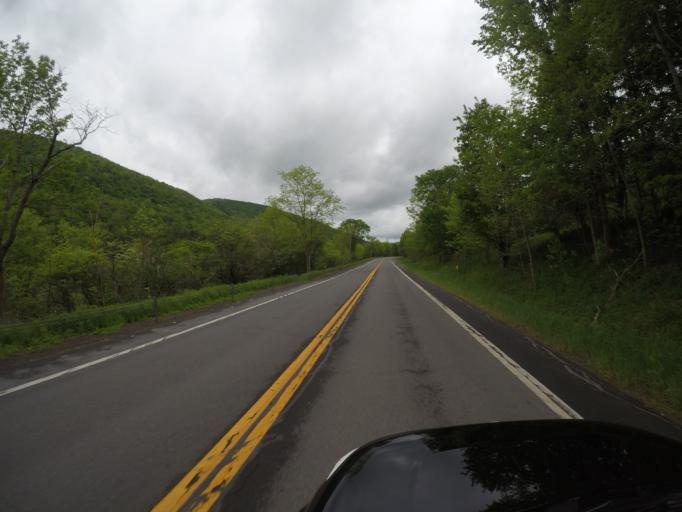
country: US
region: New York
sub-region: Delaware County
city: Delhi
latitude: 42.2504
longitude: -74.8425
